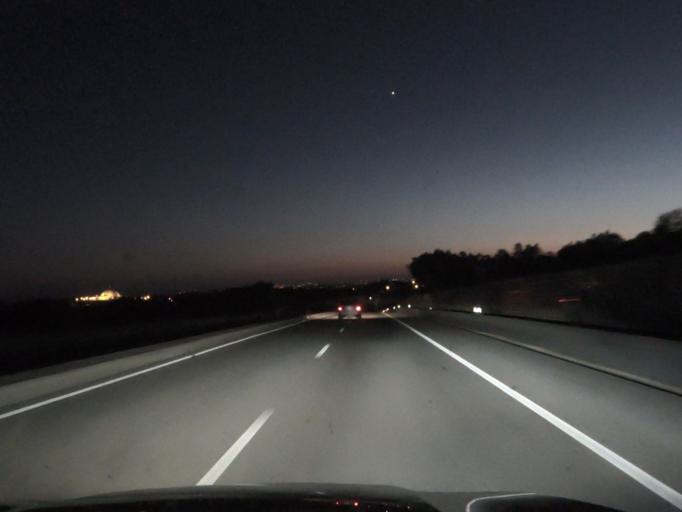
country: PT
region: Faro
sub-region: Loule
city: Loule
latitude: 37.1456
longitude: -8.0252
